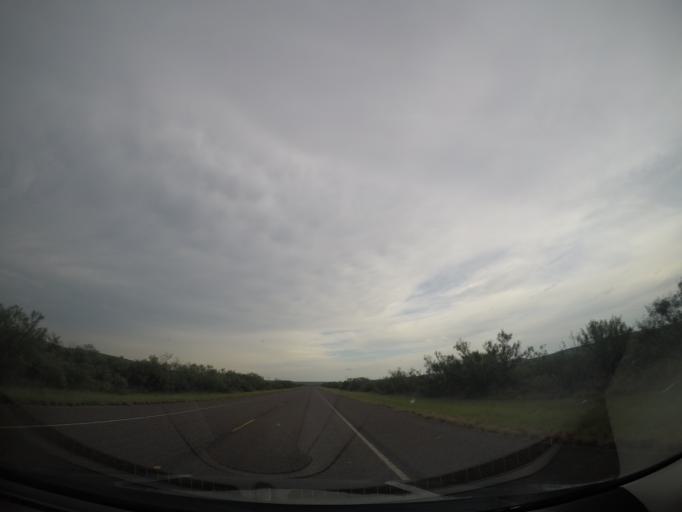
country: US
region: Texas
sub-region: Terrell County
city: Sanderson
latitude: 30.1363
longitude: -102.5773
